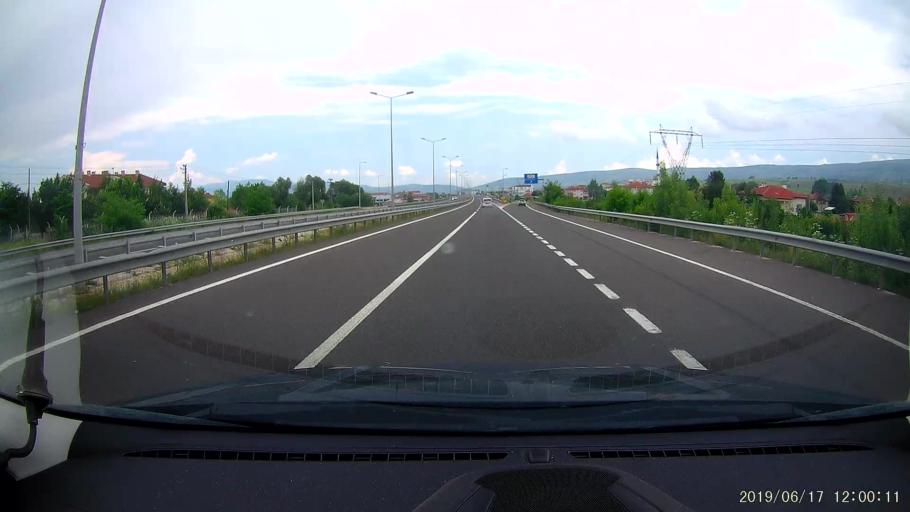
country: TR
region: Cankiri
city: Cerkes
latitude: 40.8178
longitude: 32.8979
